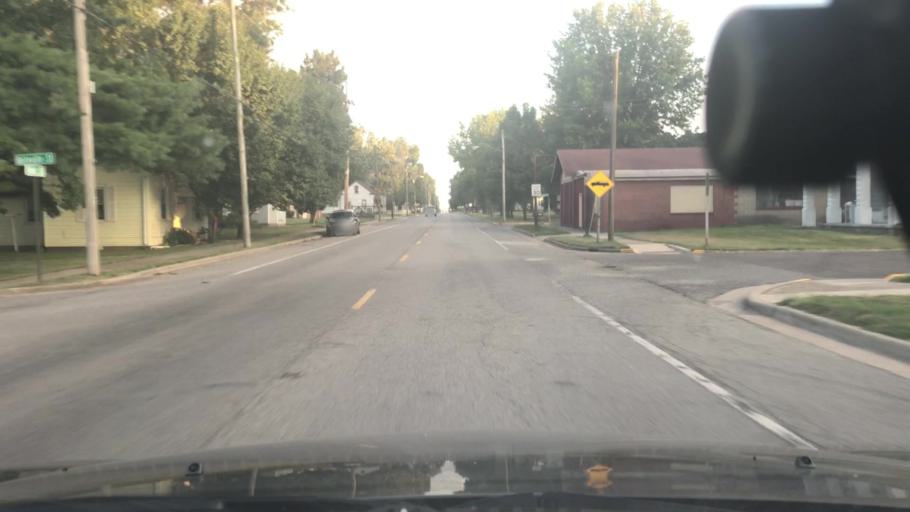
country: US
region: Illinois
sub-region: Washington County
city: Okawville
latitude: 38.4337
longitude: -89.5506
